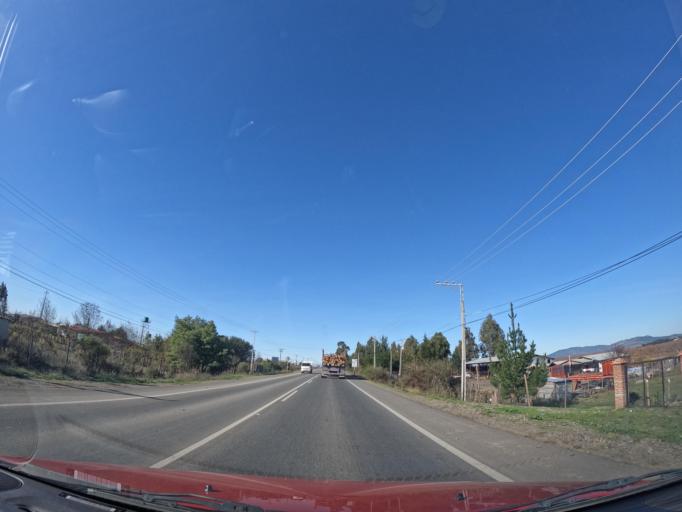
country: CL
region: Maule
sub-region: Provincia de Cauquenes
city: Cauquenes
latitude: -35.9613
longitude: -72.2529
